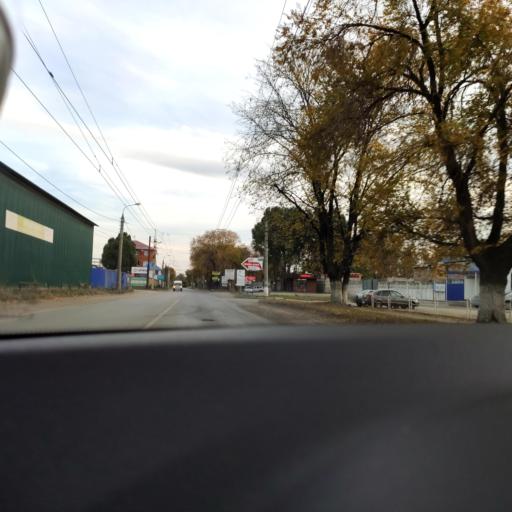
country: RU
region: Samara
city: Samara
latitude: 53.1945
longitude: 50.2730
